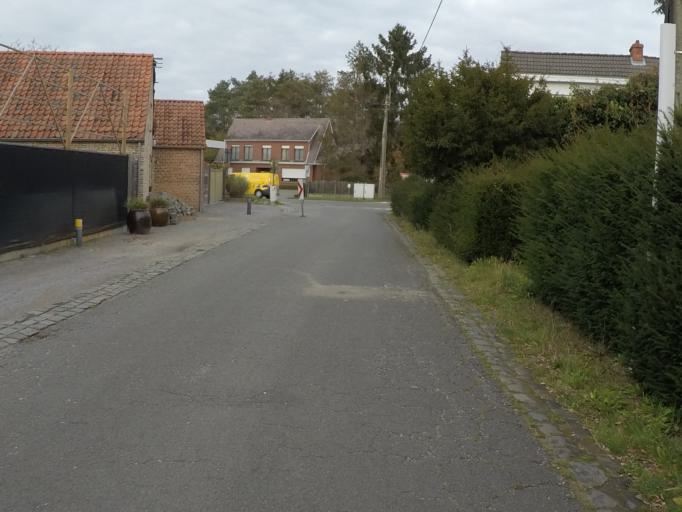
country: BE
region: Flanders
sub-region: Provincie Antwerpen
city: Nijlen
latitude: 51.1695
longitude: 4.6464
